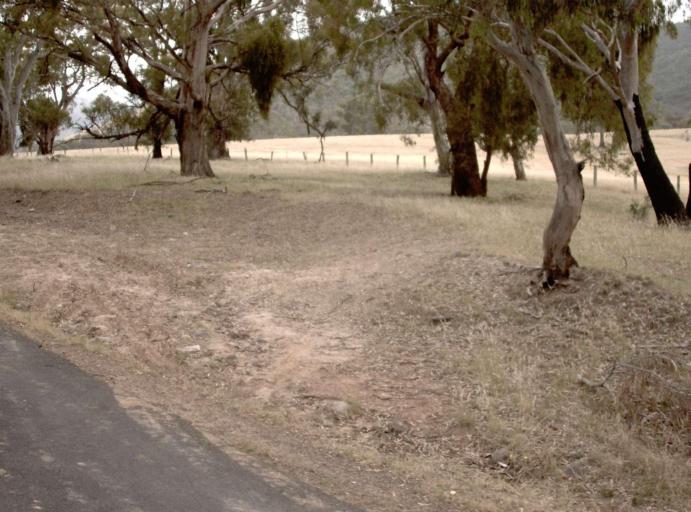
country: AU
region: Victoria
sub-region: Wellington
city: Heyfield
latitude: -37.6533
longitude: 146.6425
